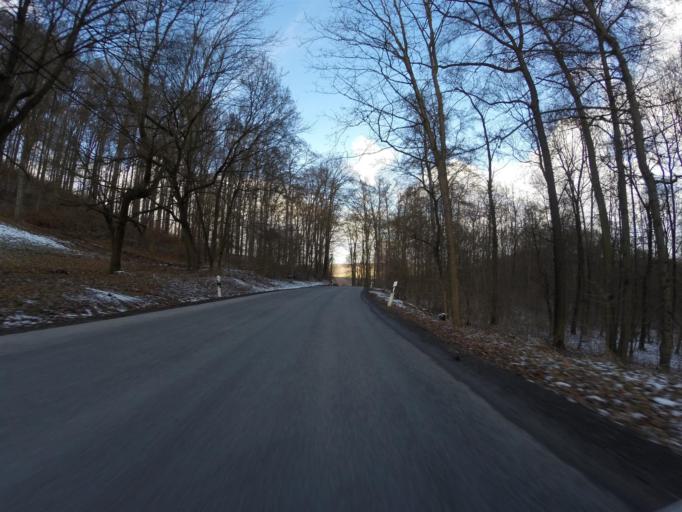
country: DE
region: Thuringia
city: Grosslobichau
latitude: 50.9377
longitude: 11.6887
